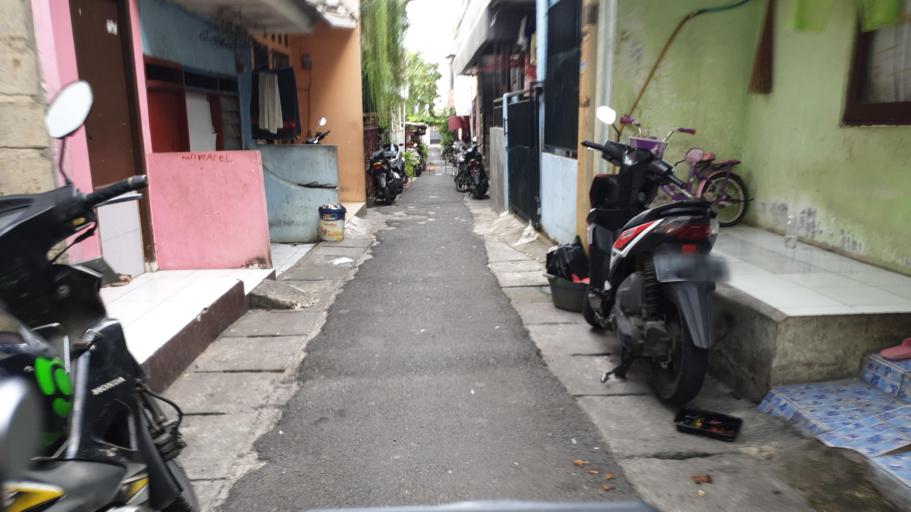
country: ID
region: Banten
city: South Tangerang
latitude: -6.2770
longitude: 106.7917
